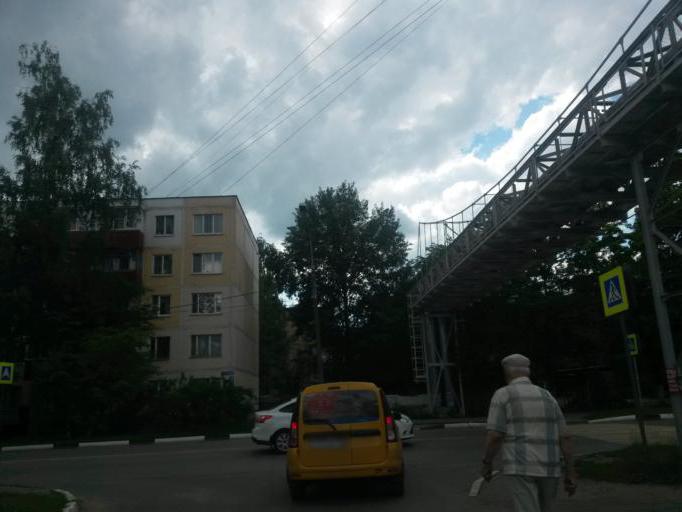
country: RU
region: Moskovskaya
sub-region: Chekhovskiy Rayon
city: Chekhov
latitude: 55.1532
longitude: 37.4788
